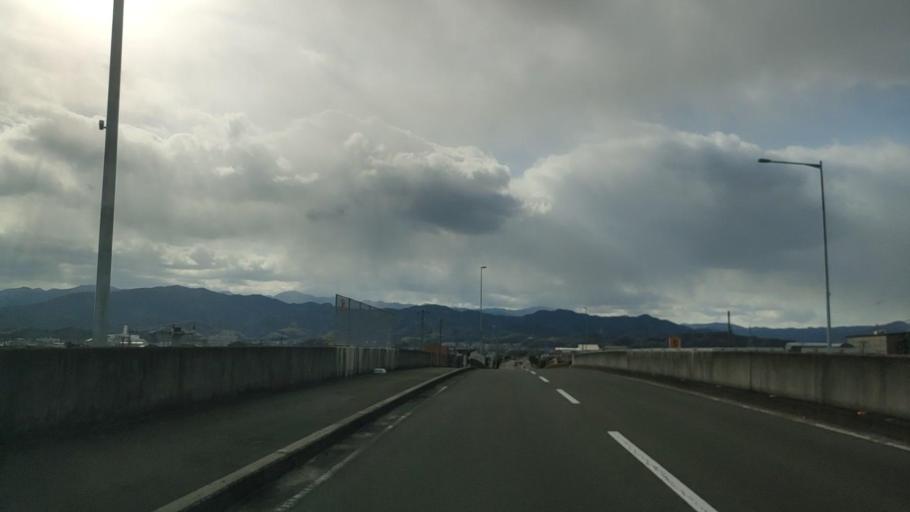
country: JP
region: Ehime
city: Saijo
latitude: 34.0448
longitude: 133.0052
